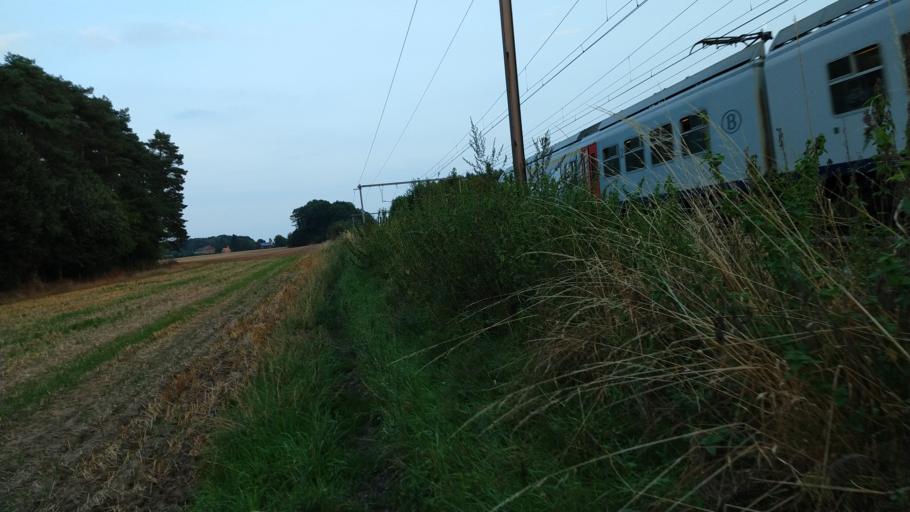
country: BE
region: Flanders
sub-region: Provincie Vlaams-Brabant
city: Boutersem
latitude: 50.8459
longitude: 4.8036
